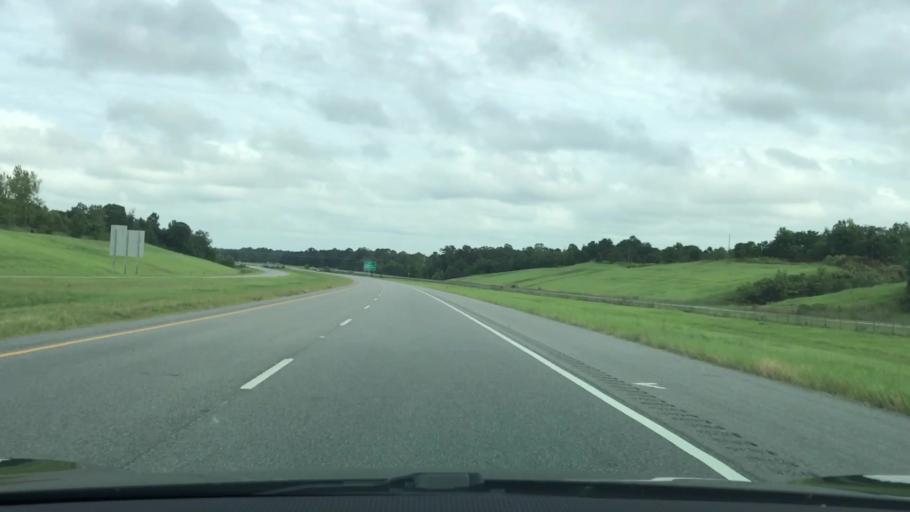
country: US
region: Alabama
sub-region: Montgomery County
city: Pike Road
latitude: 32.3488
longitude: -86.0650
